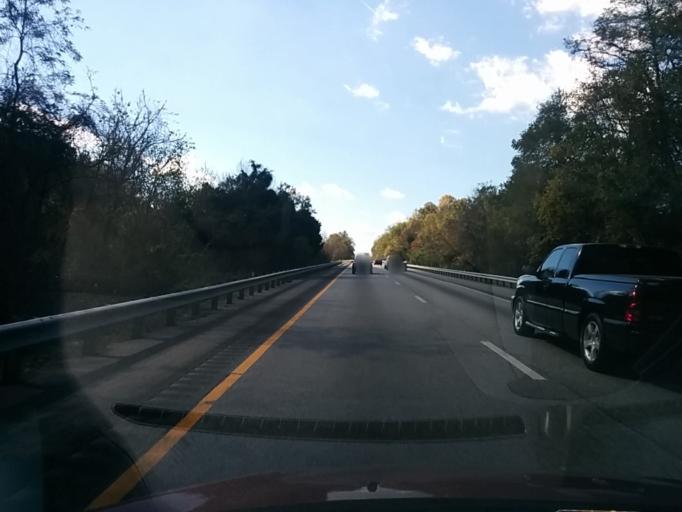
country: US
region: Virginia
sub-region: Botetourt County
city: Daleville
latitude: 37.4264
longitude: -79.8780
